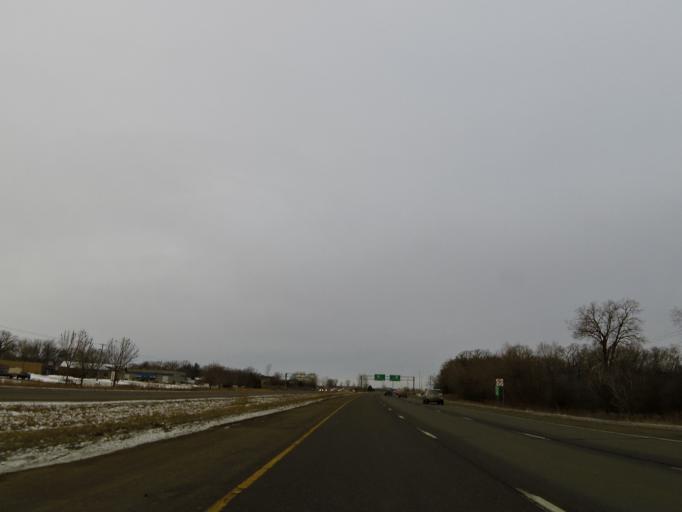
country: US
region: Minnesota
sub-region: Scott County
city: Savage
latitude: 44.7813
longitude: -93.3890
